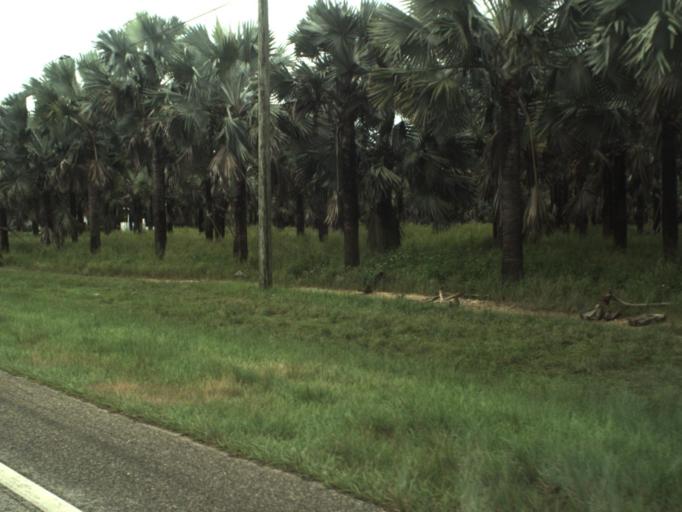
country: US
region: Florida
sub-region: Miami-Dade County
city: Richmond West
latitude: 25.5957
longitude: -80.4786
